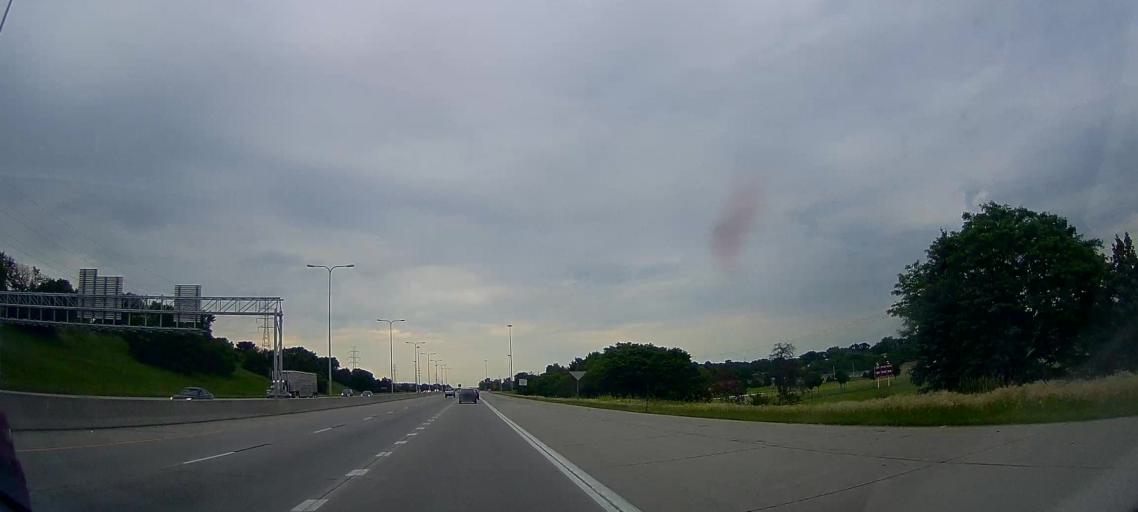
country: US
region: Nebraska
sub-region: Douglas County
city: Ralston
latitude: 41.2999
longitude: -96.0710
